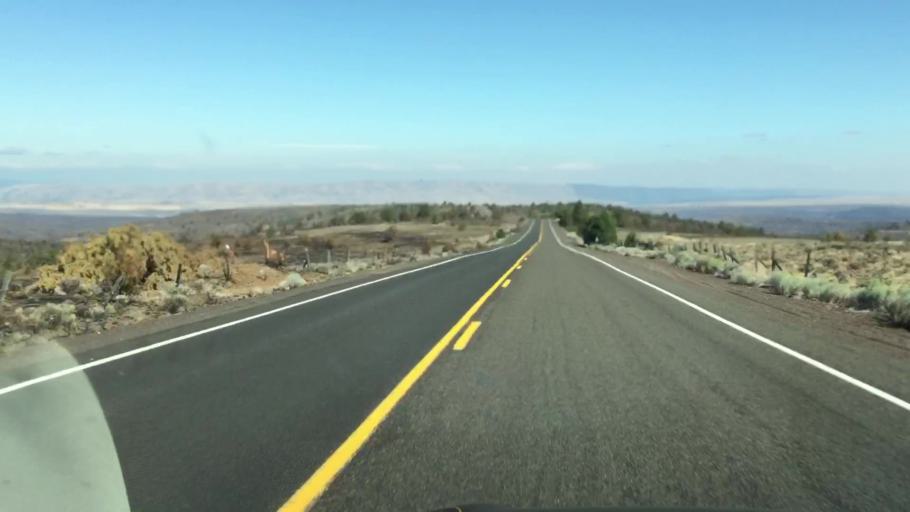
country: US
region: Oregon
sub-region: Jefferson County
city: Warm Springs
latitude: 45.0712
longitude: -121.0229
